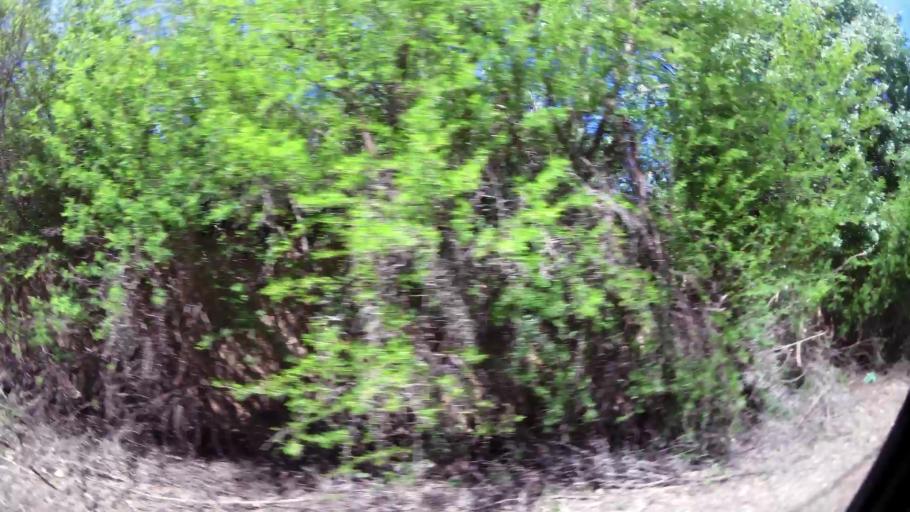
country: MA
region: Marrakech-Tensift-Al Haouz
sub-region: Marrakech
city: Marrakesh
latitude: 31.6647
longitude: -7.9583
